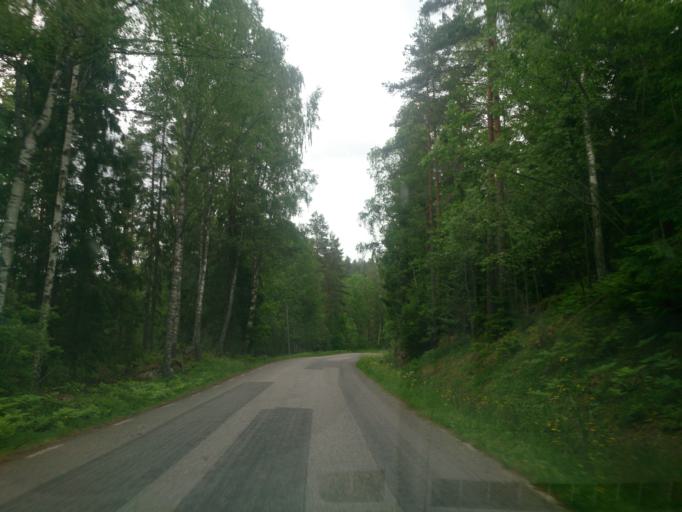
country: SE
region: OEstergoetland
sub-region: Soderkopings Kommun
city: Soederkoeping
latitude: 58.3049
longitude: 16.2675
